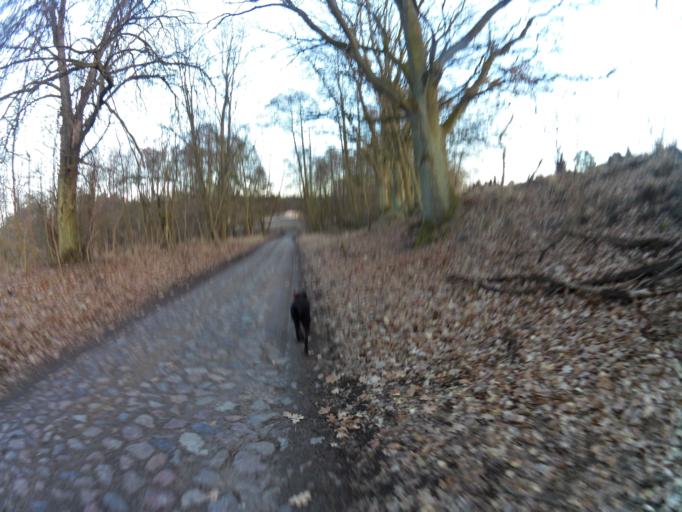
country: PL
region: West Pomeranian Voivodeship
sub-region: Powiat mysliborski
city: Debno
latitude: 52.8097
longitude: 14.7886
